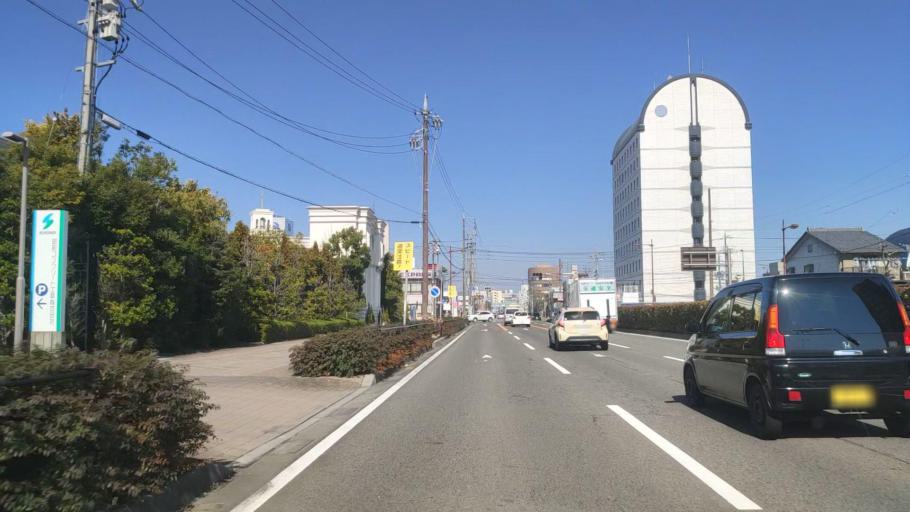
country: JP
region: Gifu
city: Gifu-shi
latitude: 35.4116
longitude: 136.7473
